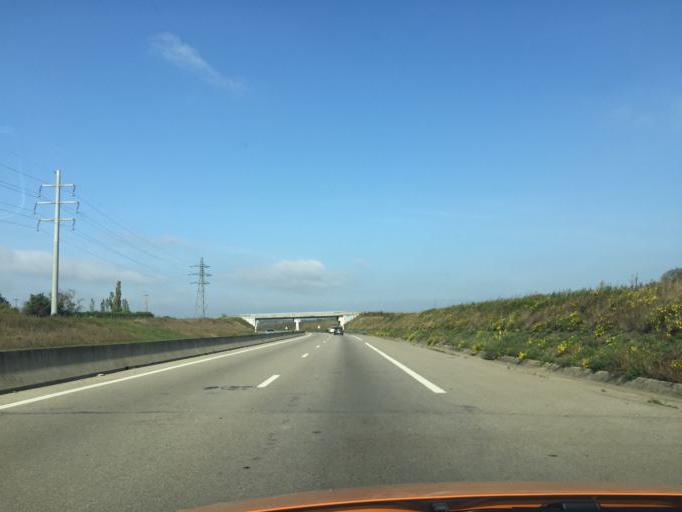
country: FR
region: Rhone-Alpes
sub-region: Departement de la Drome
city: Saint-Marcel-les-Valence
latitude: 44.9442
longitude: 4.9421
